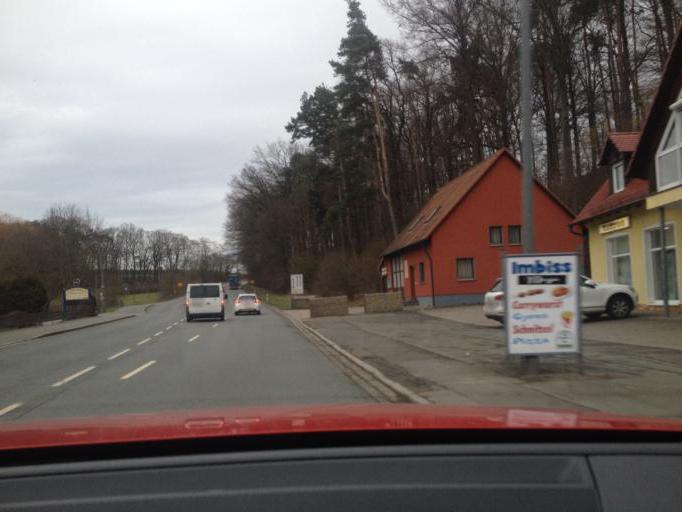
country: DE
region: Bavaria
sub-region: Regierungsbezirk Mittelfranken
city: Rohr
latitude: 49.3664
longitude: 10.8859
